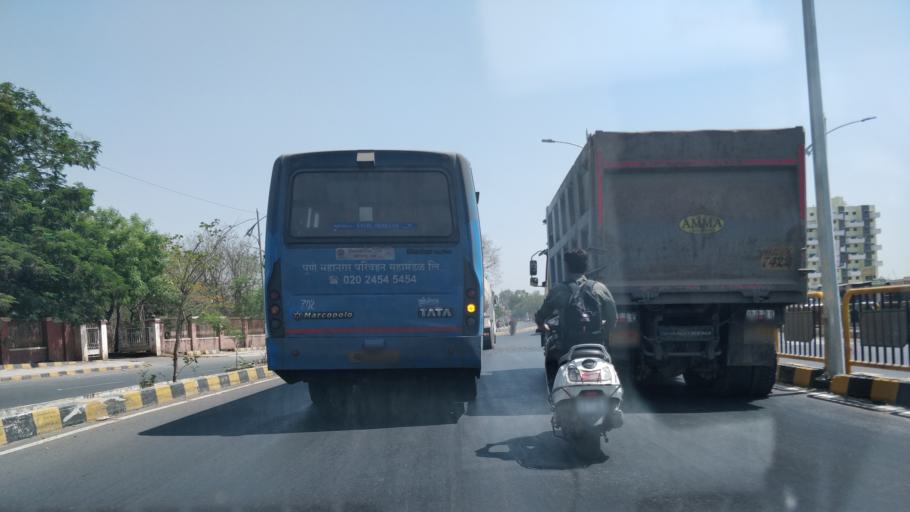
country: IN
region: Maharashtra
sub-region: Pune Division
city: Alandi
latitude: 18.6645
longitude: 73.8873
